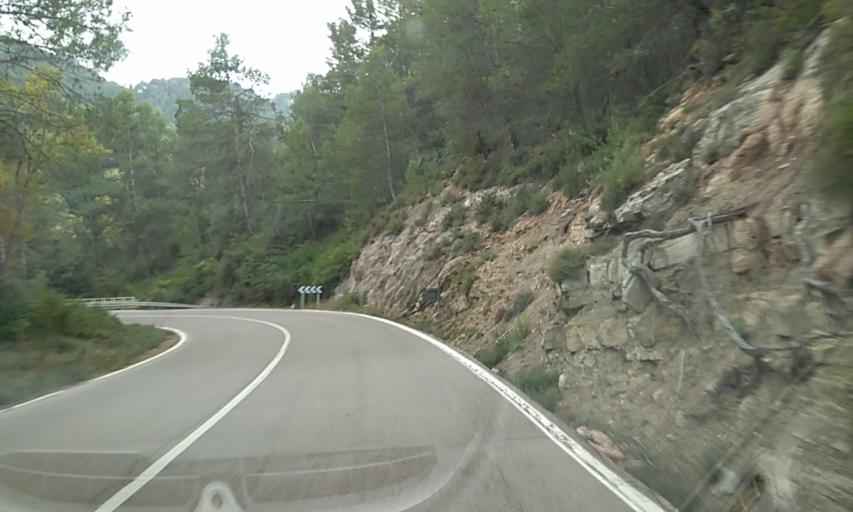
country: ES
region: Valencia
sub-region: Provincia de Castello
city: Puebla de Arenoso
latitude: 40.0872
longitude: -0.5659
